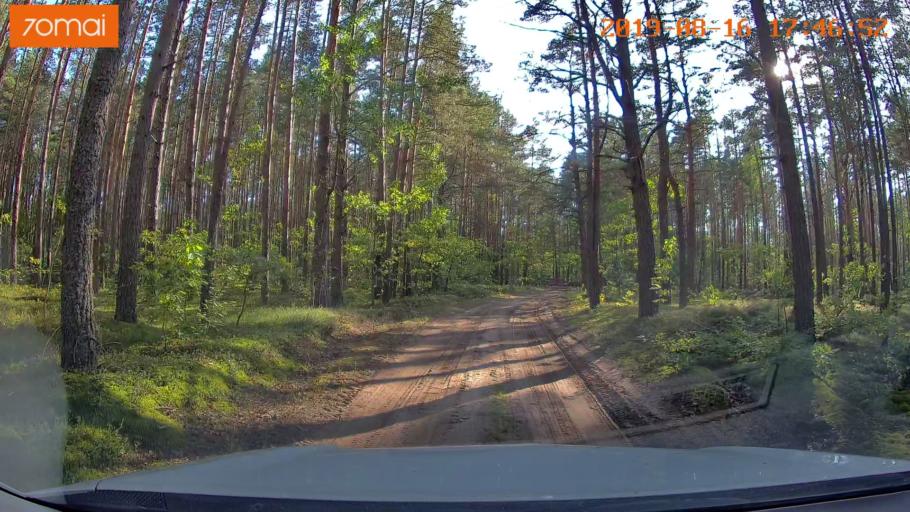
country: BY
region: Mogilev
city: Asipovichy
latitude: 53.2305
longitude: 28.6664
